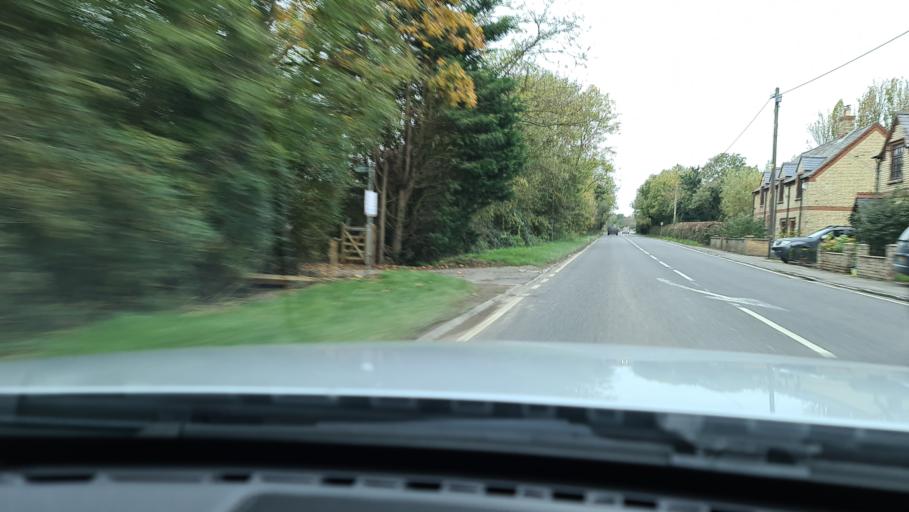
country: GB
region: England
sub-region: Buckinghamshire
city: Steeple Claydon
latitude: 51.8661
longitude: -1.0006
